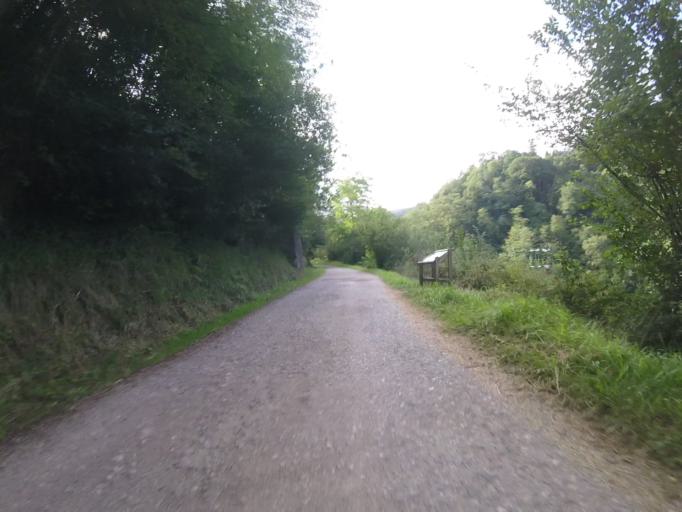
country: ES
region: Basque Country
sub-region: Provincia de Guipuzcoa
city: Andoain
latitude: 43.1936
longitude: -2.0081
